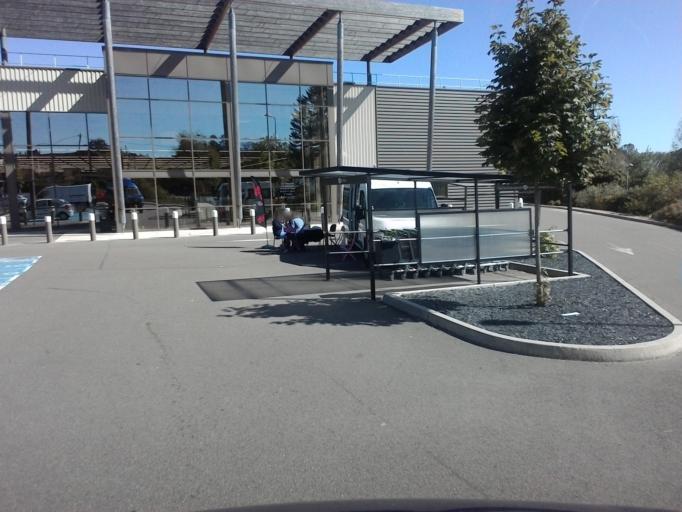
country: FR
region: Bourgogne
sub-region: Departement de la Cote-d'Or
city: Saulieu
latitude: 47.2806
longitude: 4.2362
